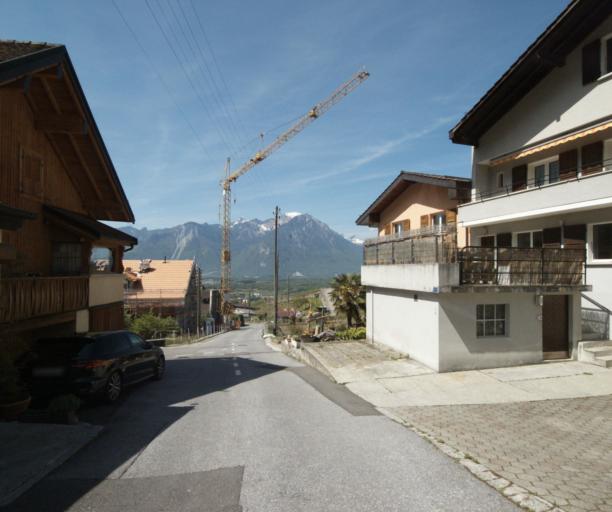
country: CH
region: Vaud
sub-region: Aigle District
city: Villeneuve
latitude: 46.4006
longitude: 6.9398
